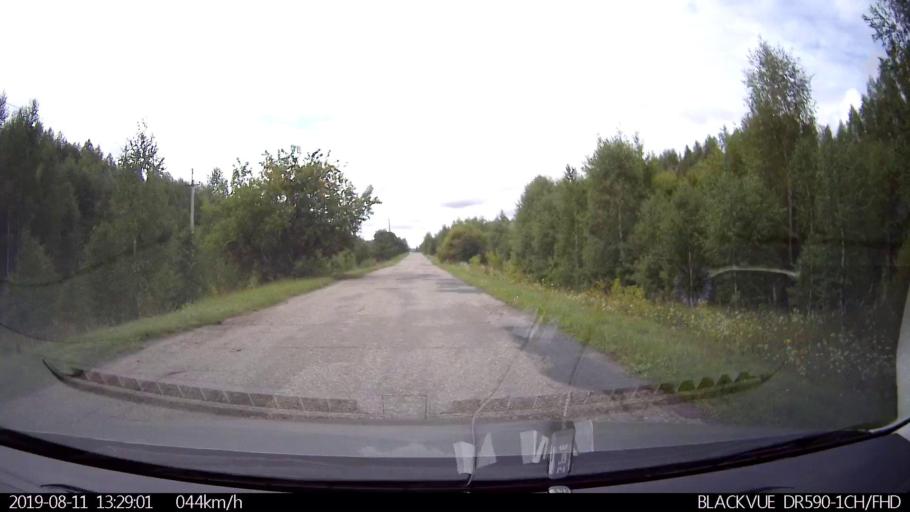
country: RU
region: Ulyanovsk
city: Ignatovka
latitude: 53.8594
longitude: 47.6192
